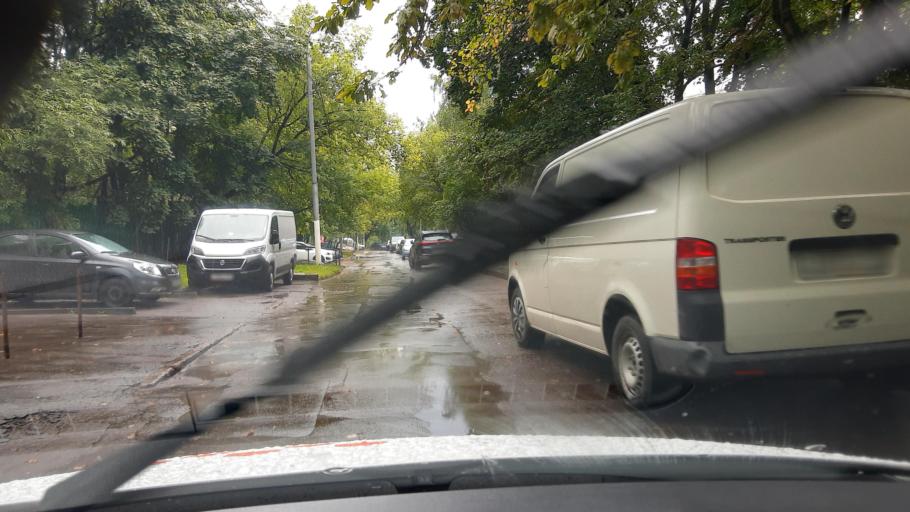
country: RU
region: Moscow
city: Tsaritsyno
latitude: 55.6210
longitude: 37.6488
